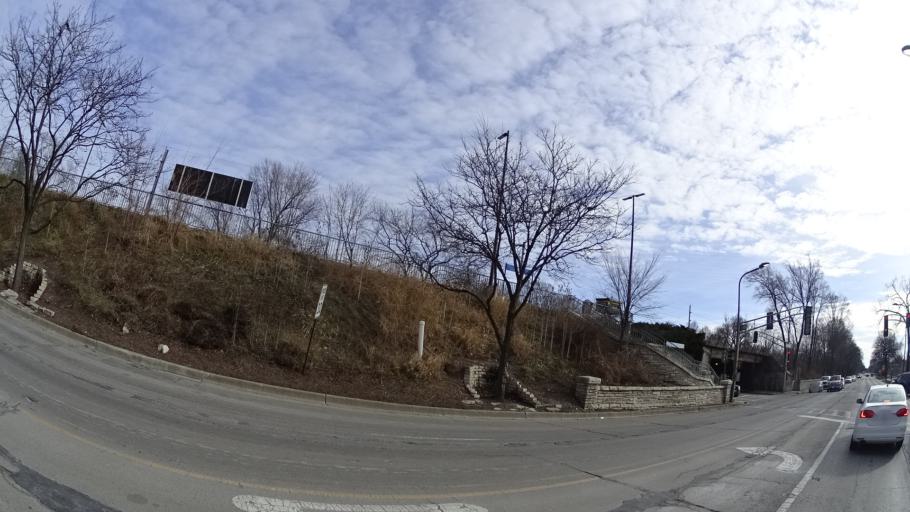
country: US
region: Illinois
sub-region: Cook County
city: Evanston
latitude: 42.0625
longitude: -87.6973
